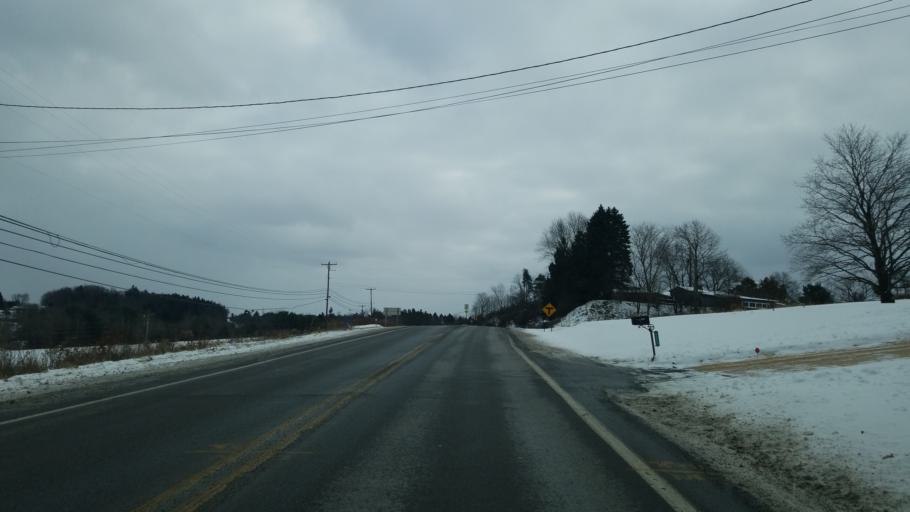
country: US
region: Pennsylvania
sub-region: Clearfield County
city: Sandy
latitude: 41.0807
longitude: -78.7599
